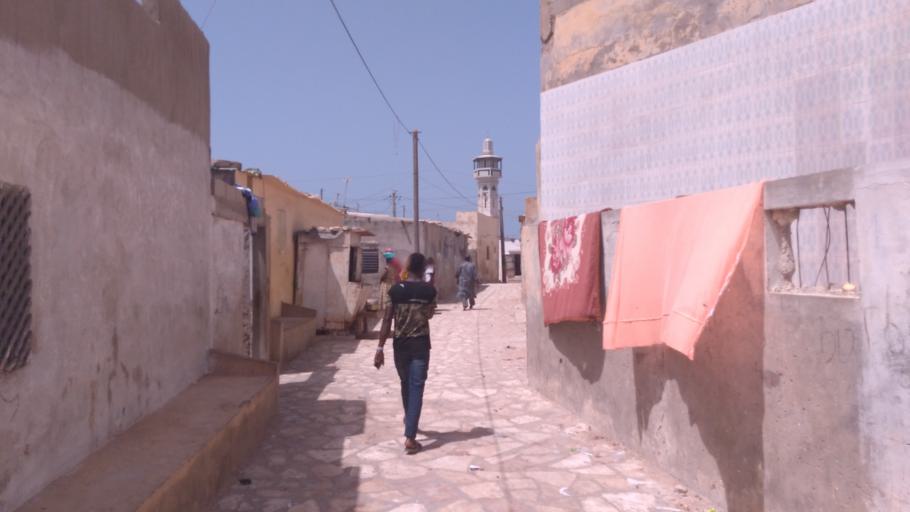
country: SN
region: Dakar
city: Pikine
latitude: 14.6869
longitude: -17.2271
